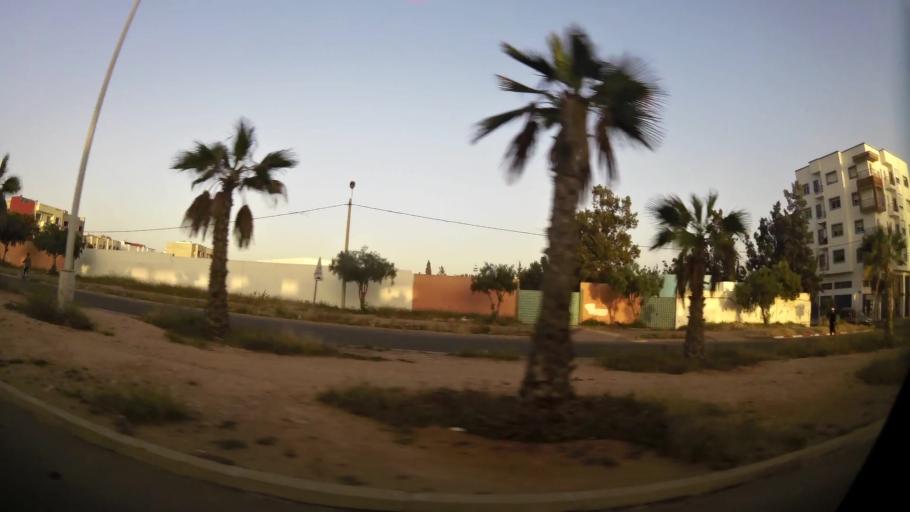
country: MA
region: Oued ed Dahab-Lagouira
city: Dakhla
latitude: 30.3952
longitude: -9.5651
